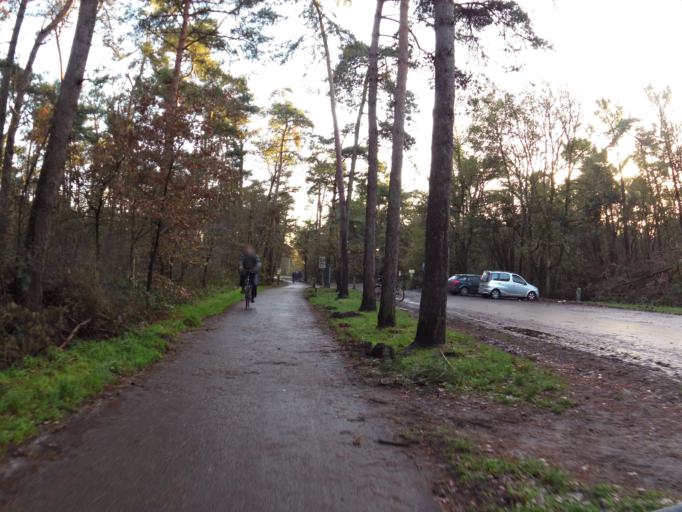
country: NL
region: North Brabant
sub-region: Gemeente Waalwijk
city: Waalwijk
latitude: 51.6568
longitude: 5.0713
